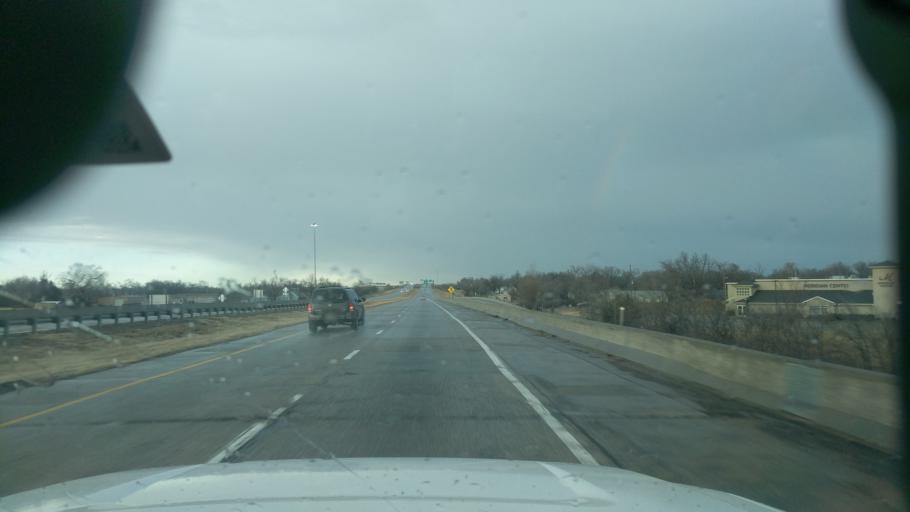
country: US
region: Kansas
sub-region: Harvey County
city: Newton
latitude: 38.0505
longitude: -97.3224
